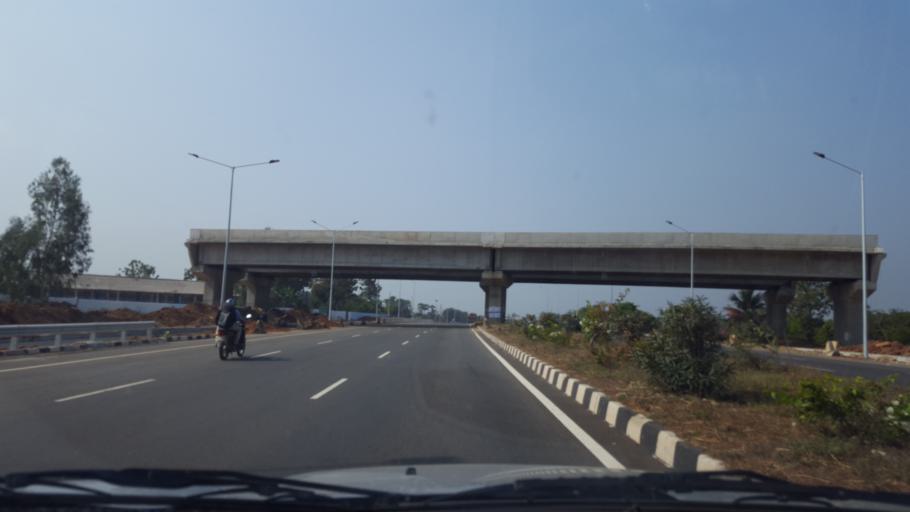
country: IN
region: Andhra Pradesh
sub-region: Vishakhapatnam
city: Bhimunipatnam
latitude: 17.9953
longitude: 83.4723
